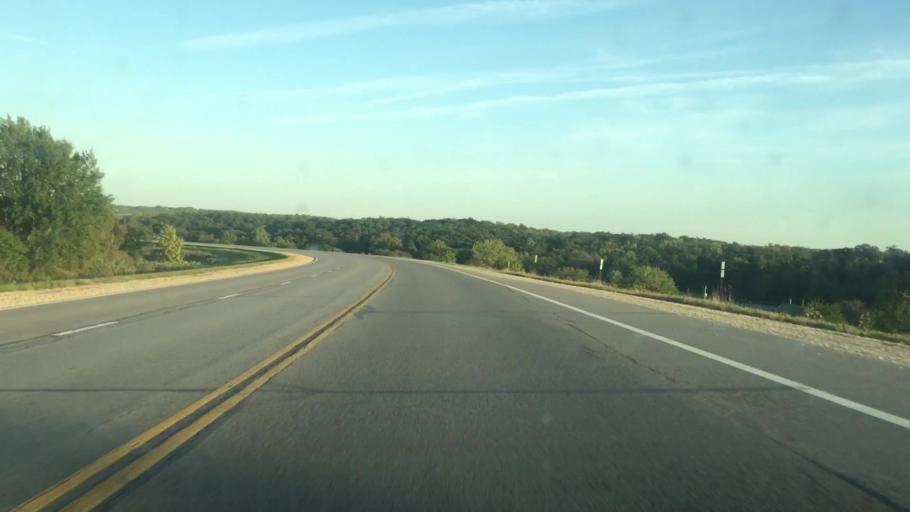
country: US
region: Kansas
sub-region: Atchison County
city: Atchison
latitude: 39.4867
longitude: -95.1282
